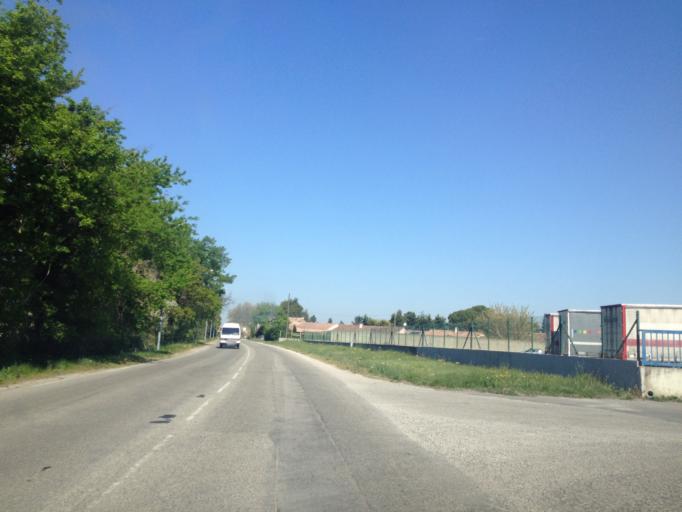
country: FR
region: Provence-Alpes-Cote d'Azur
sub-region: Departement du Vaucluse
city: Jonquieres
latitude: 44.1124
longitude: 4.9106
